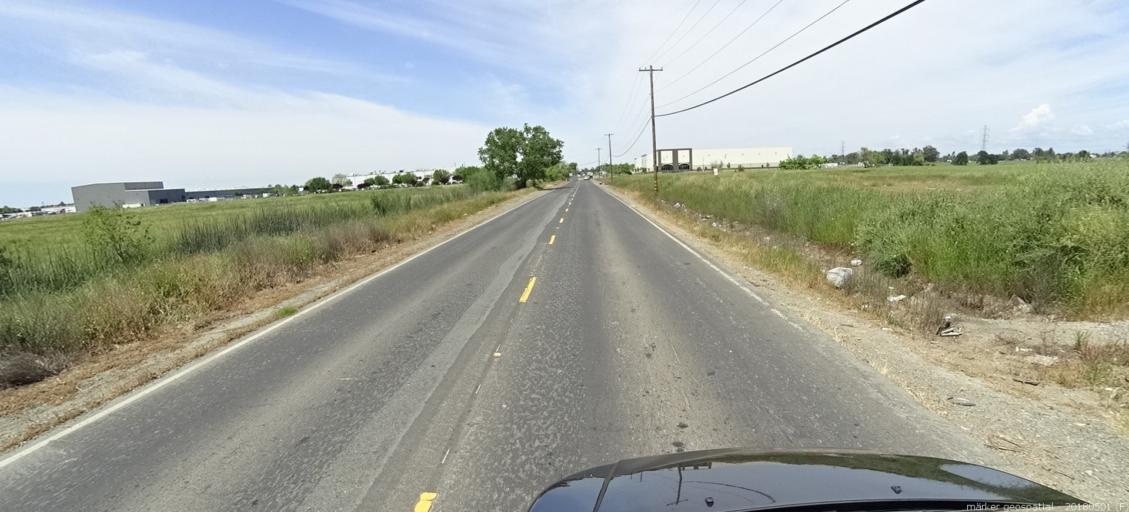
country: US
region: California
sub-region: Sacramento County
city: Rio Linda
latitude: 38.6612
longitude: -121.4292
